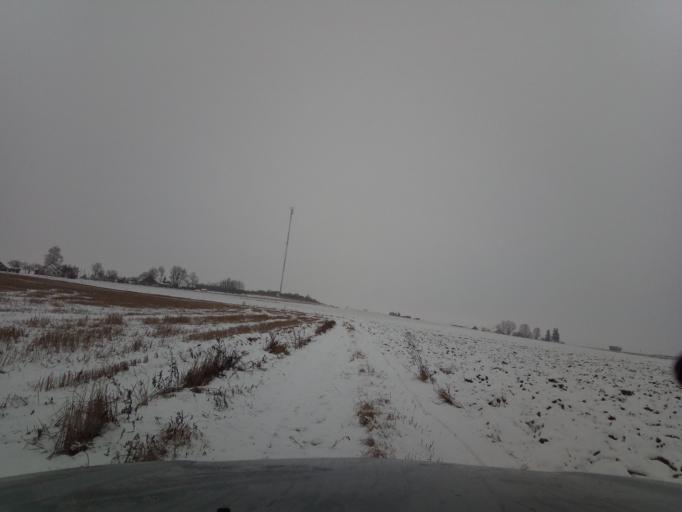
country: LT
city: Ramygala
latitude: 55.4843
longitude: 24.2930
